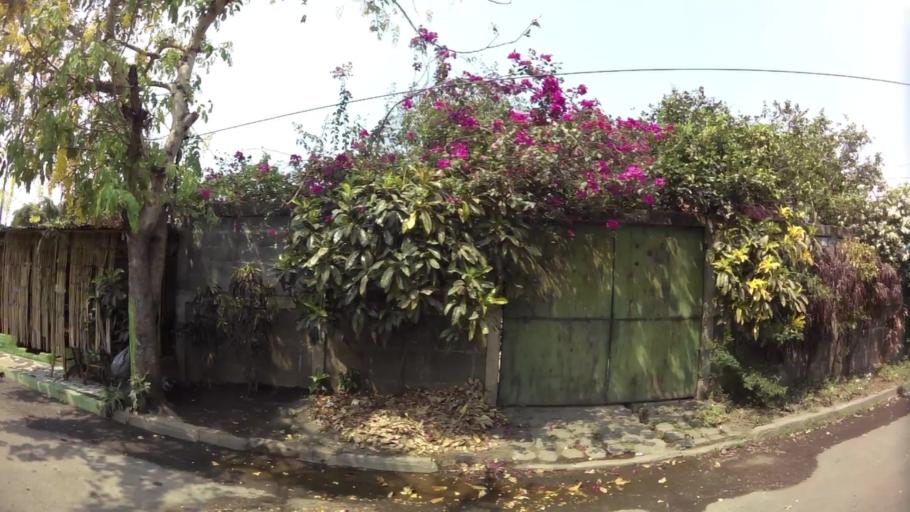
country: NI
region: Managua
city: Ciudad Sandino
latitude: 12.1265
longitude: -86.3148
